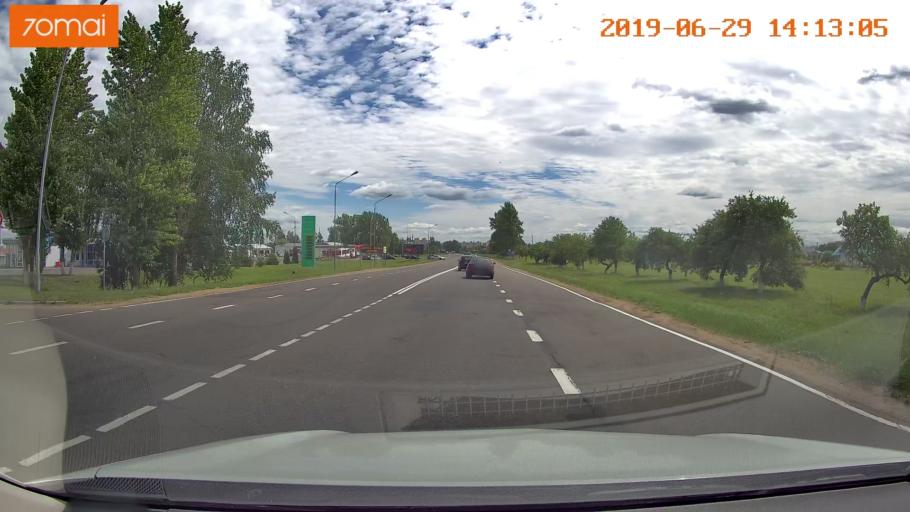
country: BY
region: Minsk
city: Salihorsk
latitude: 52.8051
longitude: 27.5096
